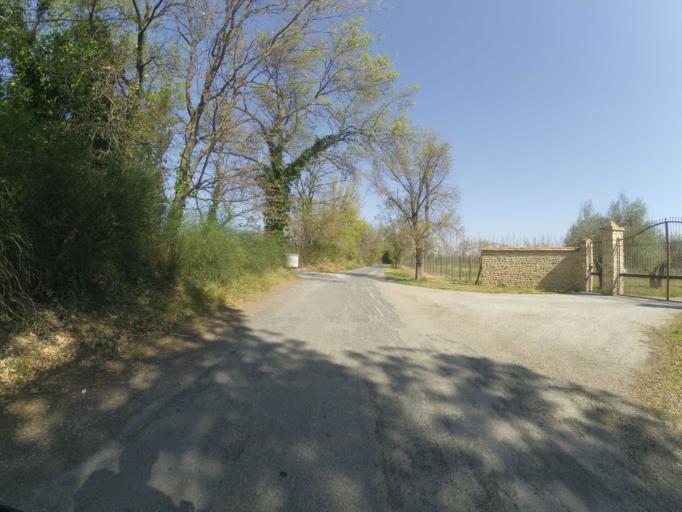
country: FR
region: Languedoc-Roussillon
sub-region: Departement des Pyrenees-Orientales
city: Thuir
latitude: 42.6641
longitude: 2.7590
